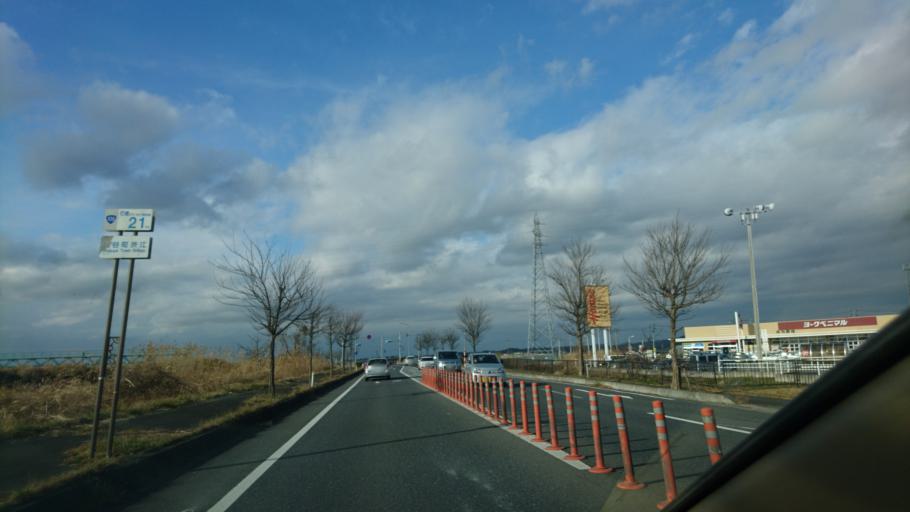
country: JP
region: Miyagi
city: Wakuya
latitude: 38.5369
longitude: 141.1183
